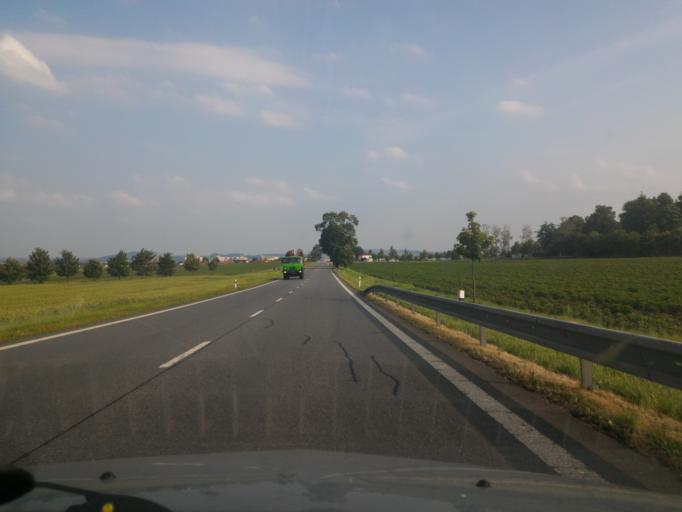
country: CZ
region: Vysocina
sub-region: Okres Havlickuv Brod
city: Havlickuv Brod
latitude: 49.6256
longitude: 15.5707
